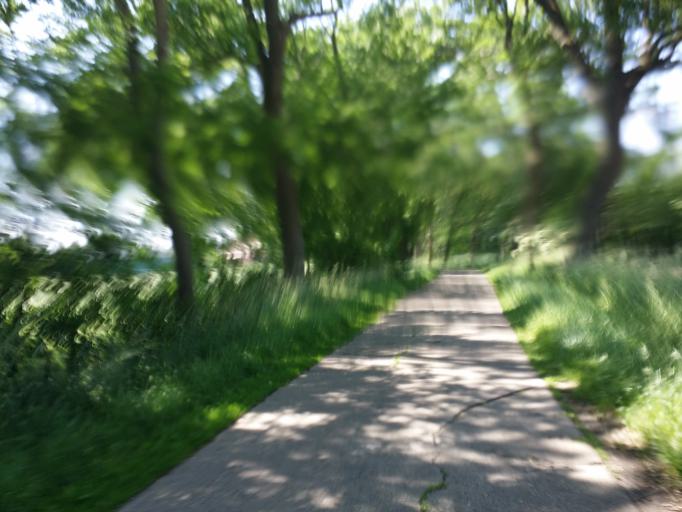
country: DE
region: Lower Saxony
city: Neuenkirchen
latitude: 53.1623
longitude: 8.5160
